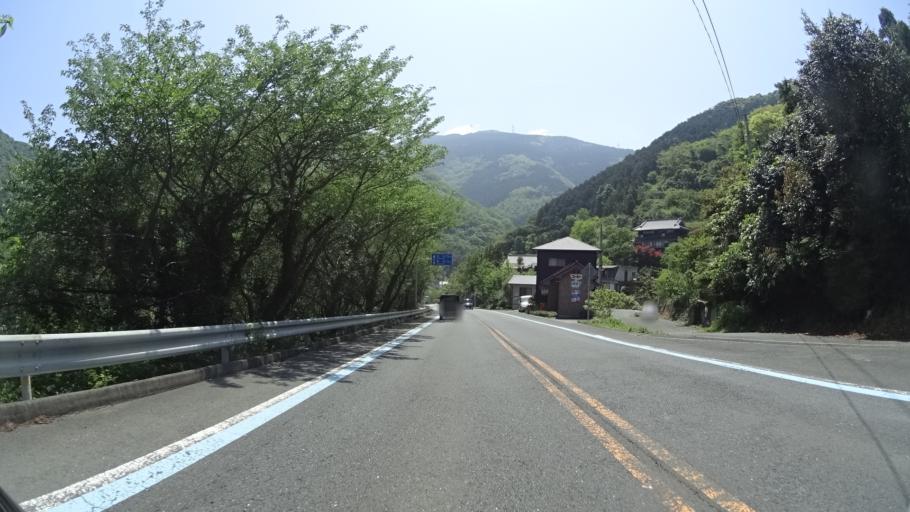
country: JP
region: Ehime
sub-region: Nishiuwa-gun
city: Ikata-cho
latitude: 33.5383
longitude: 132.4049
